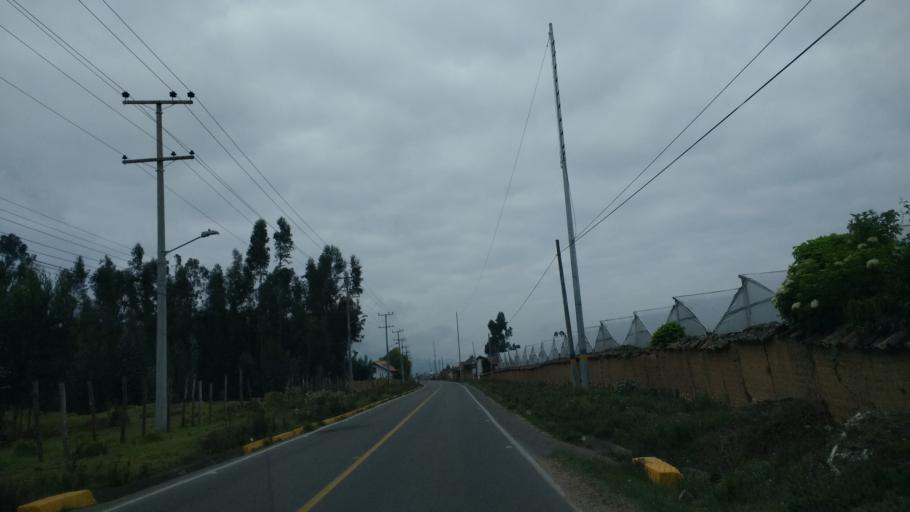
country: CO
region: Cundinamarca
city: Suesca
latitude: 5.0821
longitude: -73.7926
